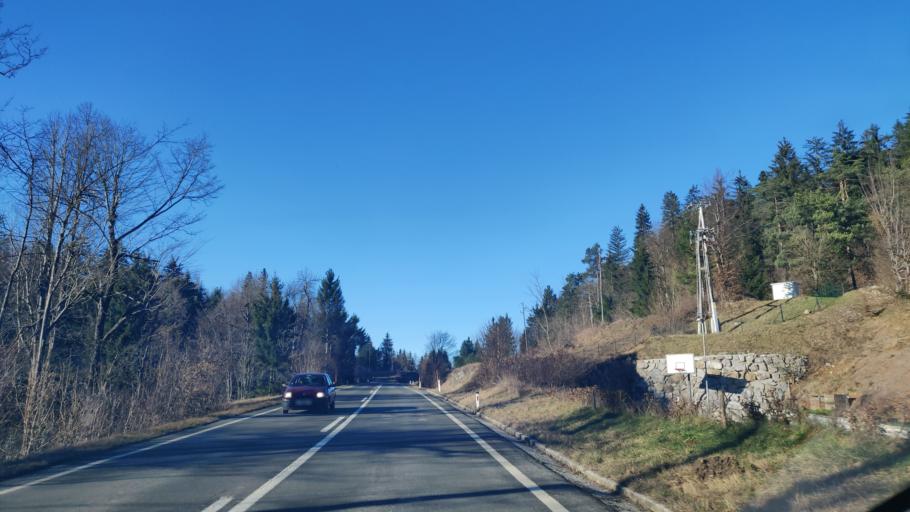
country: SI
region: Logatec
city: Logatec
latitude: 45.8805
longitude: 14.2064
